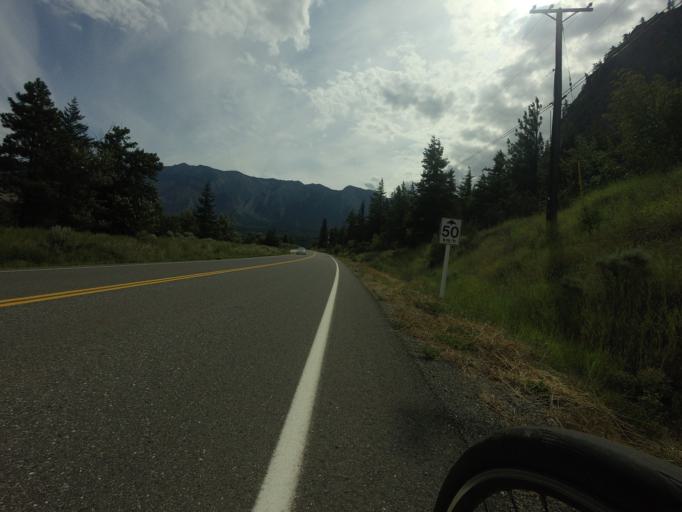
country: CA
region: British Columbia
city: Lillooet
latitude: 50.6701
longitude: -121.9506
